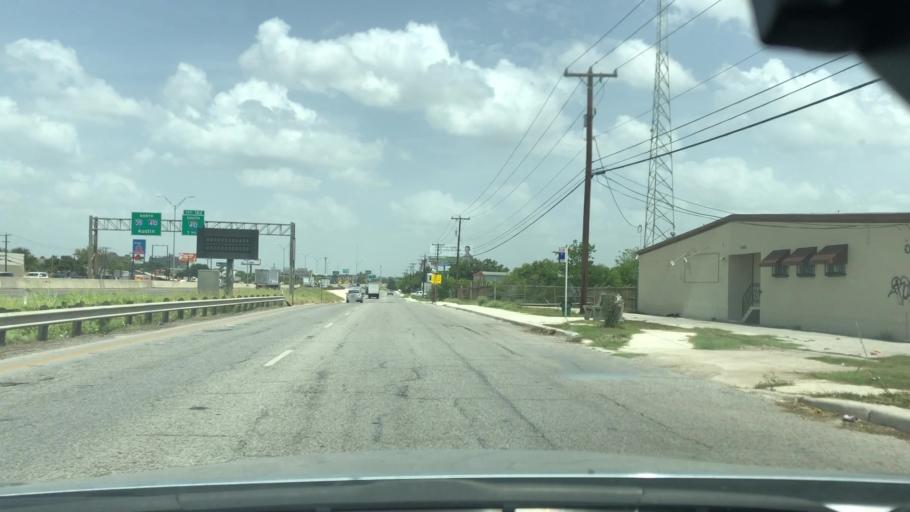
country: US
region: Texas
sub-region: Bexar County
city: Terrell Hills
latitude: 29.4460
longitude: -98.4302
